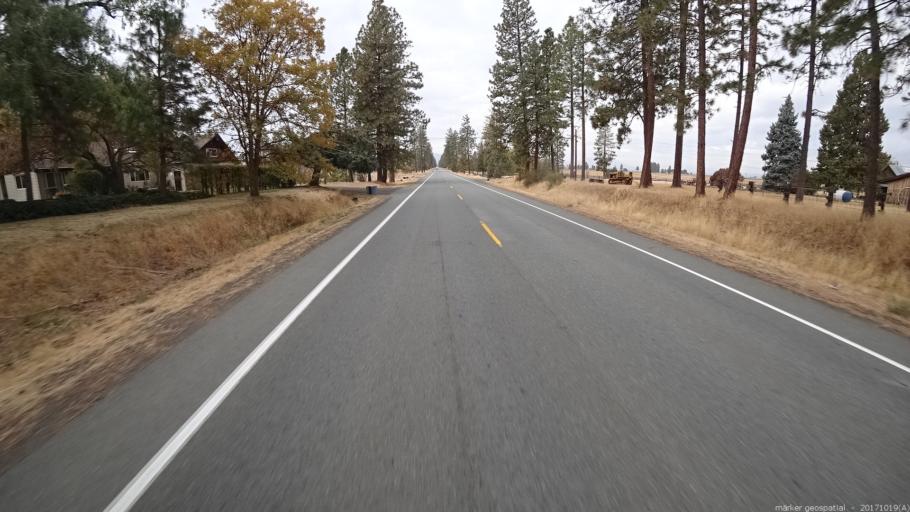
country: US
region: California
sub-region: Shasta County
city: Burney
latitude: 41.0674
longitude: -121.3489
